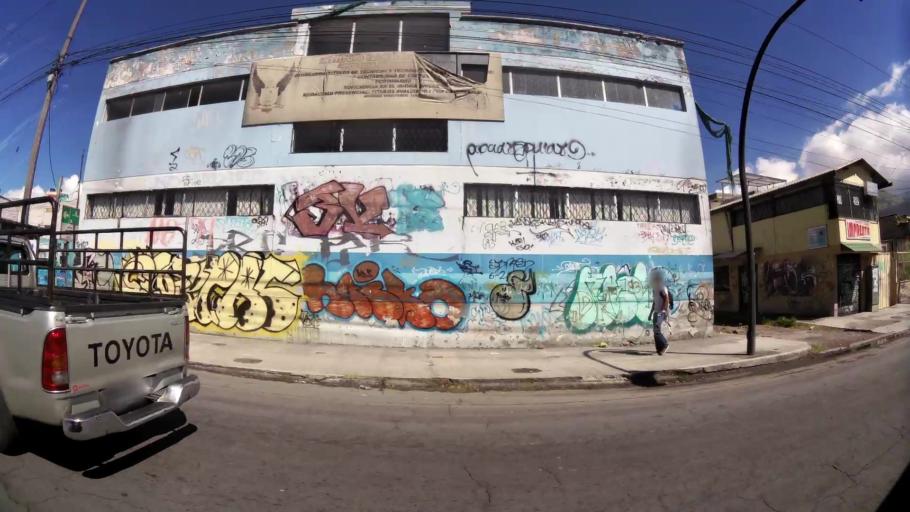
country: EC
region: Pichincha
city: Quito
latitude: -0.2534
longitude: -78.5312
